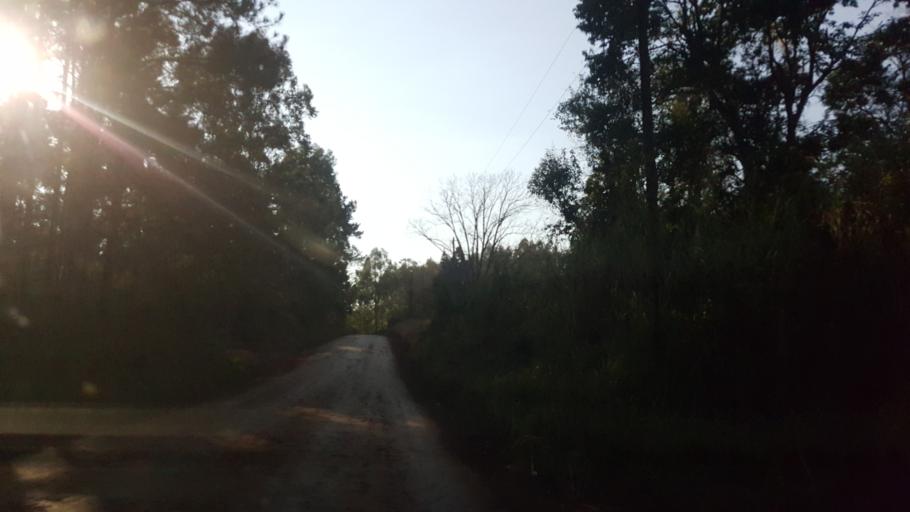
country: AR
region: Misiones
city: Capiovi
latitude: -26.8906
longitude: -55.0681
